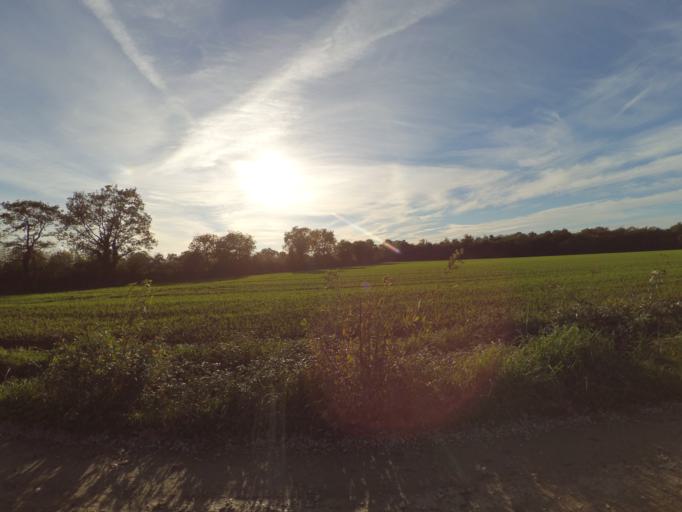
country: FR
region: Pays de la Loire
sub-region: Departement de la Vendee
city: Saint-Hilaire-de-Loulay
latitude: 47.0098
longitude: -1.3452
